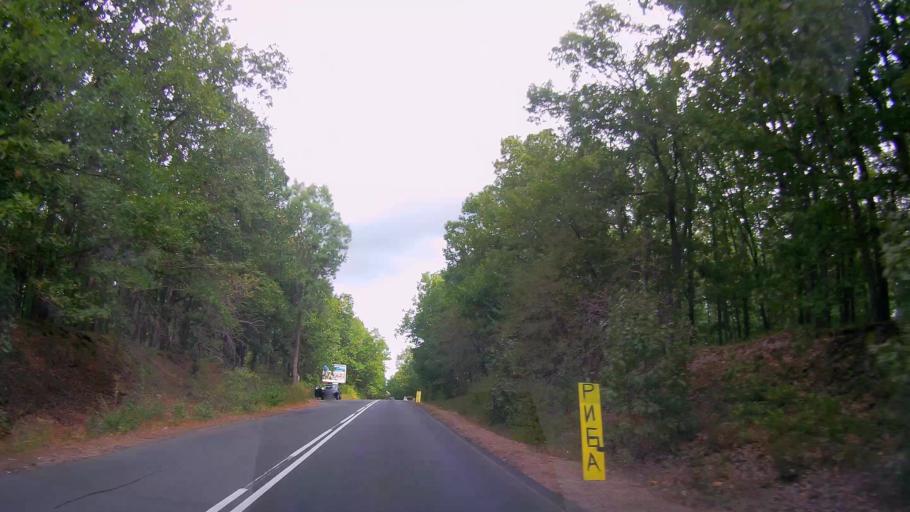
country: BG
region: Burgas
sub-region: Obshtina Primorsko
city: Primorsko
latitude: 42.2827
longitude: 27.7377
